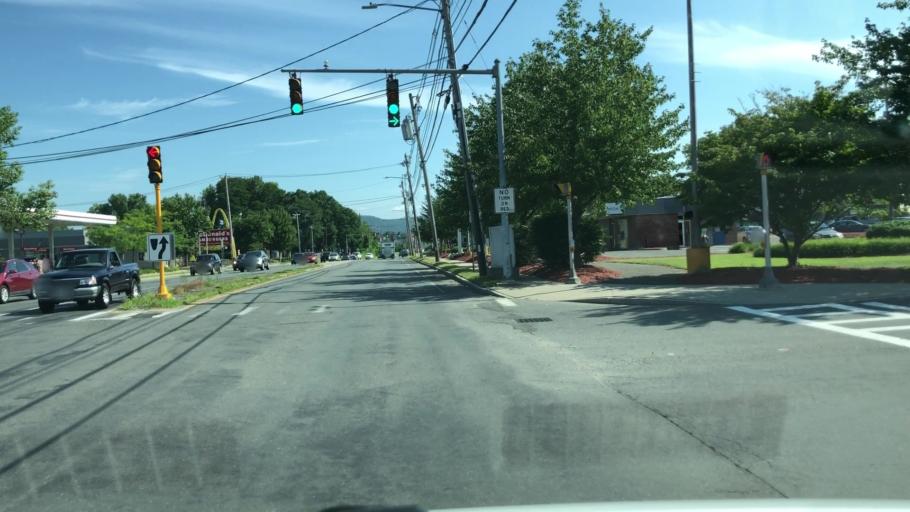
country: US
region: Massachusetts
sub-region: Hampshire County
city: Northampton
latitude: 42.3299
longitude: -72.6340
